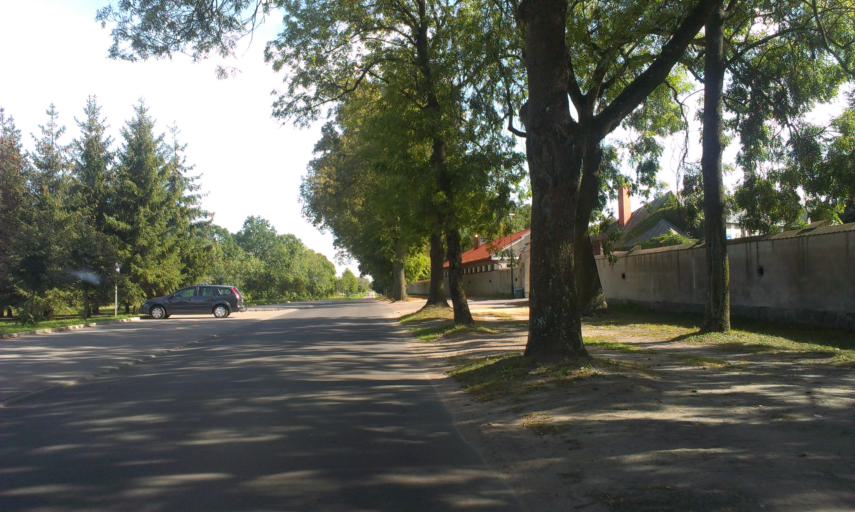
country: PL
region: Greater Poland Voivodeship
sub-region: Powiat pilski
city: Lobzenica
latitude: 53.2708
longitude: 17.2369
